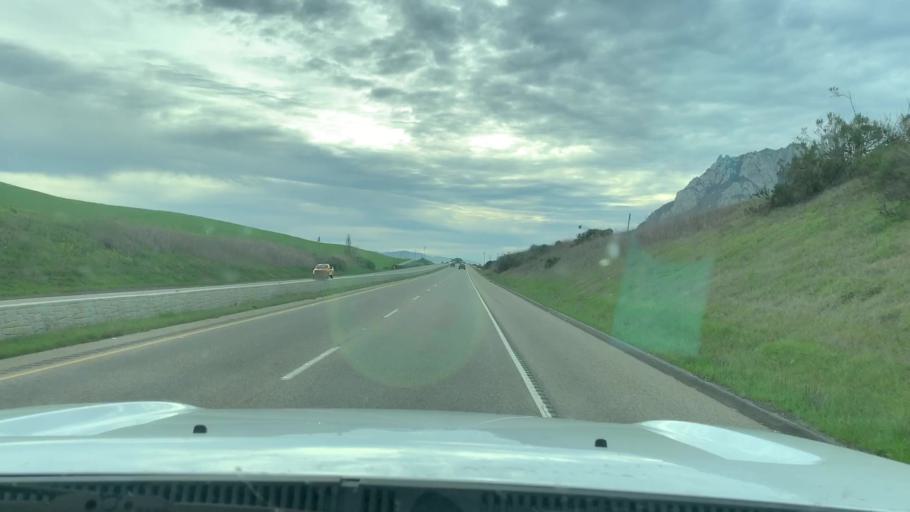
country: US
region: California
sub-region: San Luis Obispo County
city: Morro Bay
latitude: 35.3610
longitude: -120.8047
